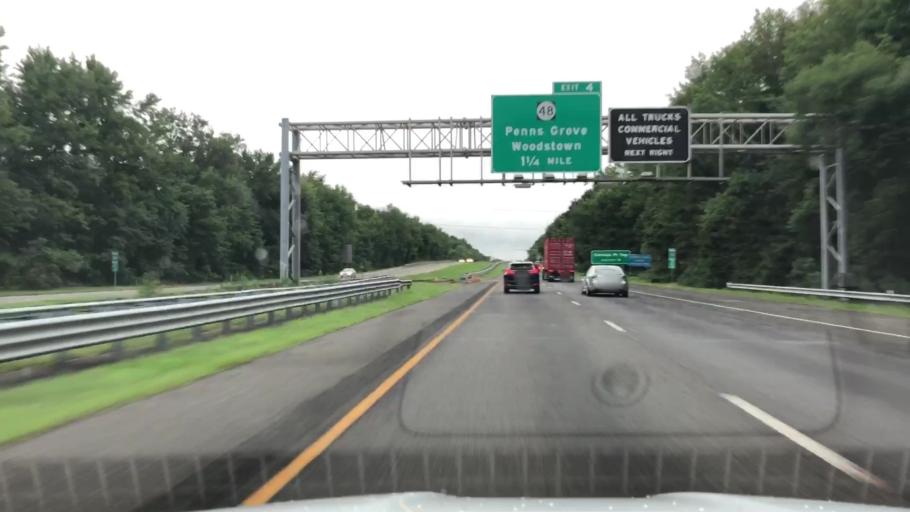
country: US
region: New Jersey
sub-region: Salem County
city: Carneys Point
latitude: 39.6925
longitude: -75.4701
